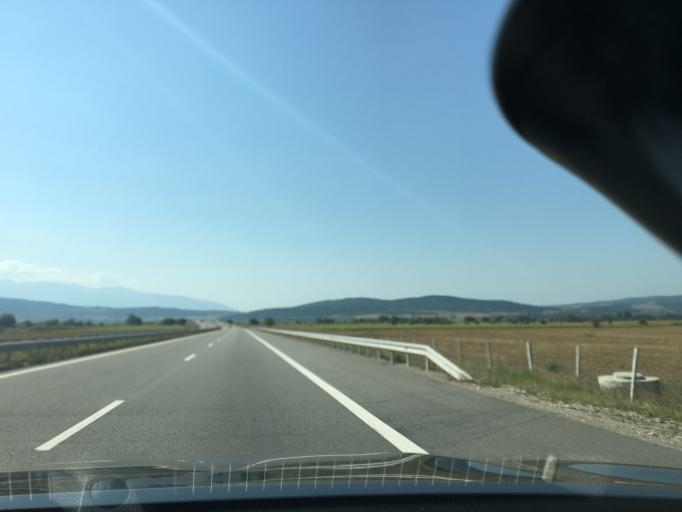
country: BG
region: Kyustendil
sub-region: Obshtina Bobovdol
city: Bobovdol
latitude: 42.4418
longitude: 23.1119
